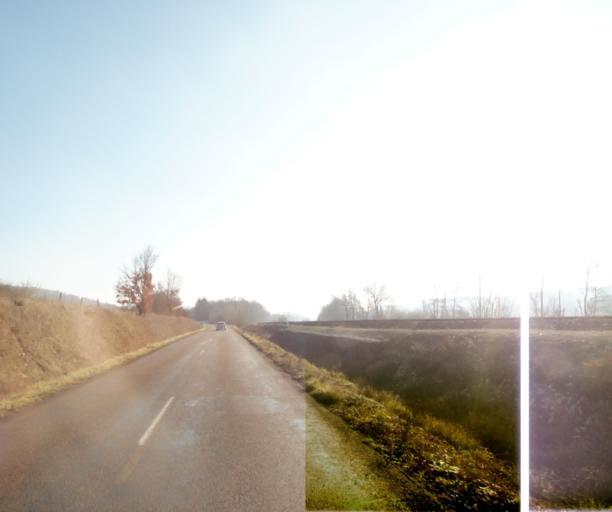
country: FR
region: Champagne-Ardenne
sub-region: Departement de la Haute-Marne
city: Chevillon
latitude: 48.5036
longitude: 5.1267
